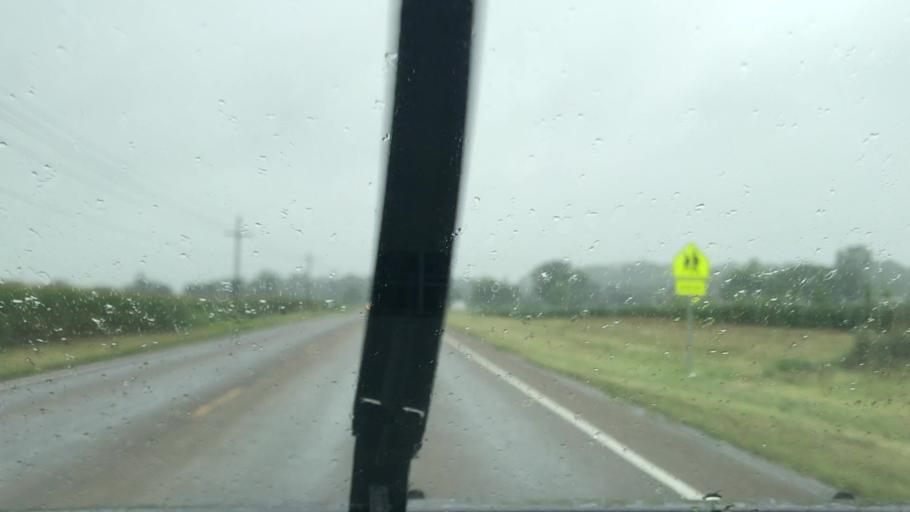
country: US
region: Indiana
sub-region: Hamilton County
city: Sheridan
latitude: 40.1203
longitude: -86.1875
